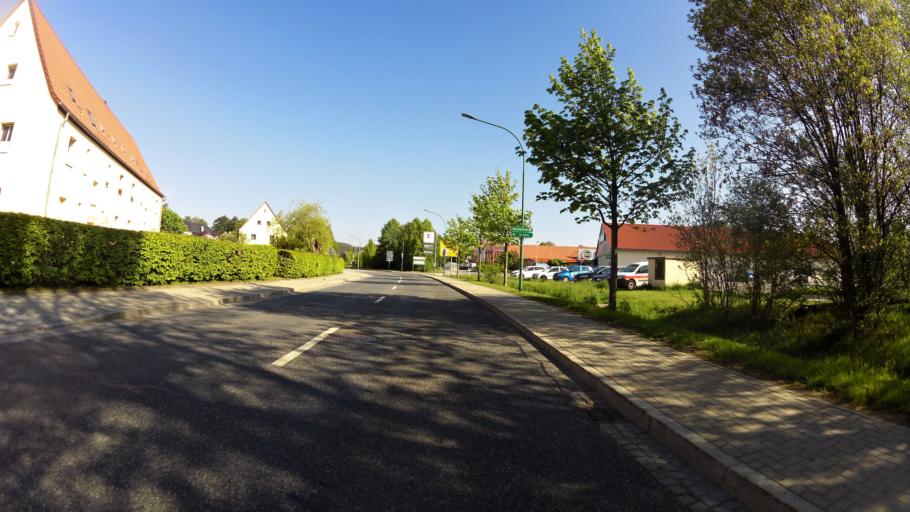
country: DE
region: Saxony
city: Neustadt in Sachsen
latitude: 51.0267
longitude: 14.2190
